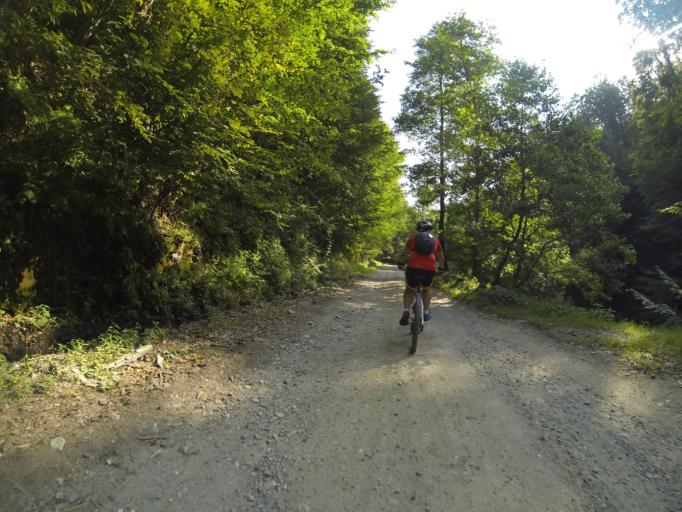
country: RO
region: Valcea
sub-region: Comuna Costesti
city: Bistrita
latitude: 45.2095
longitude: 23.9988
